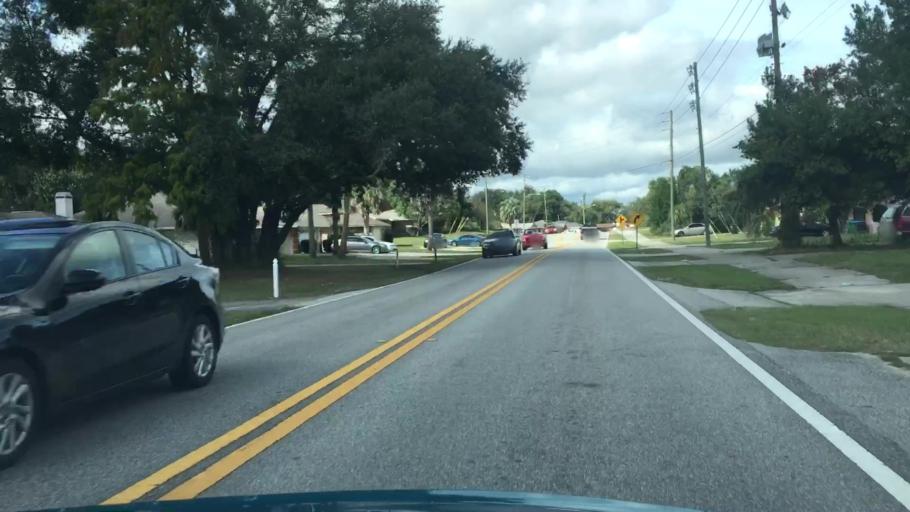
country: US
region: Florida
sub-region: Volusia County
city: Deltona
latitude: 28.8926
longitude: -81.2478
